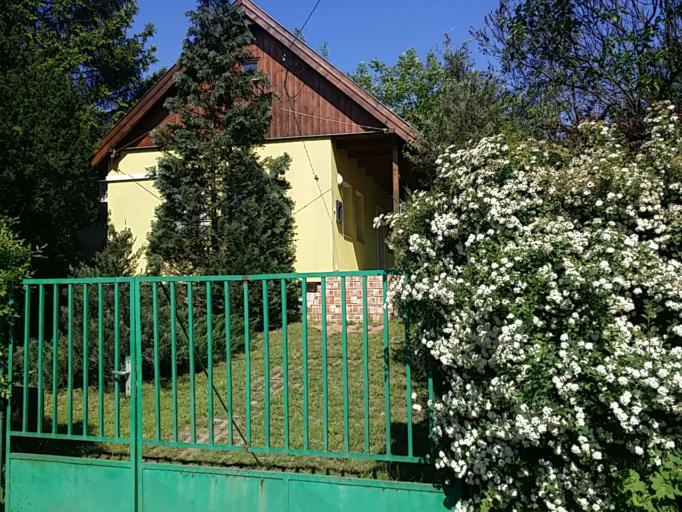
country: HU
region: Pest
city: Szada
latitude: 47.6354
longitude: 19.3283
